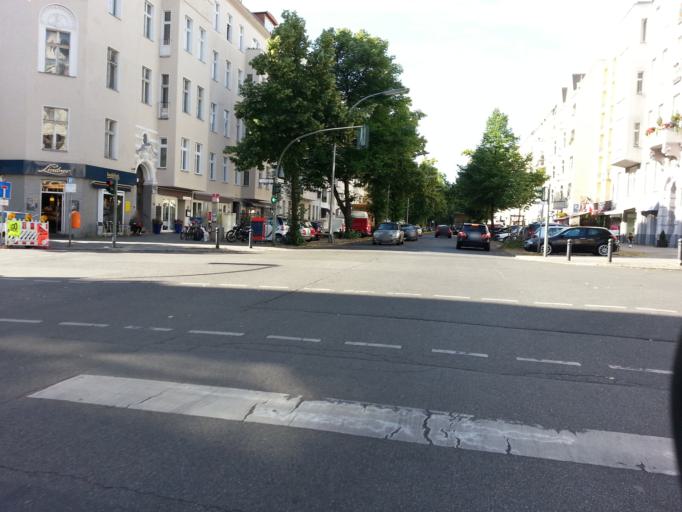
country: DE
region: Berlin
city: Hansaviertel
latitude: 52.5090
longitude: 13.3229
